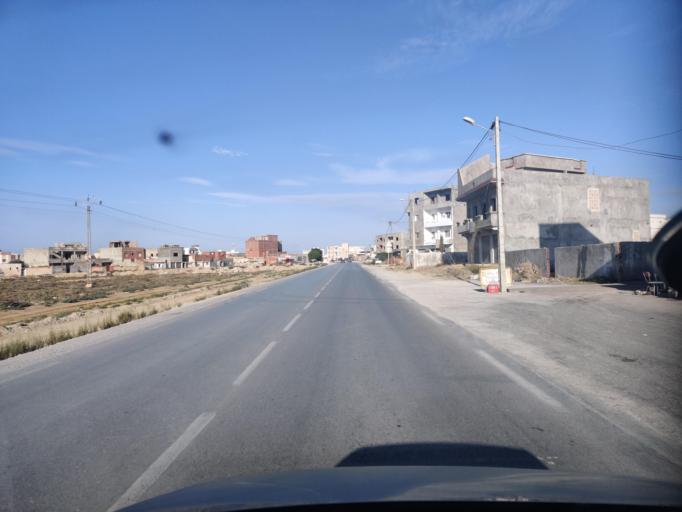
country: TN
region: Ariana
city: Ariana
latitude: 36.9555
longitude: 10.2259
